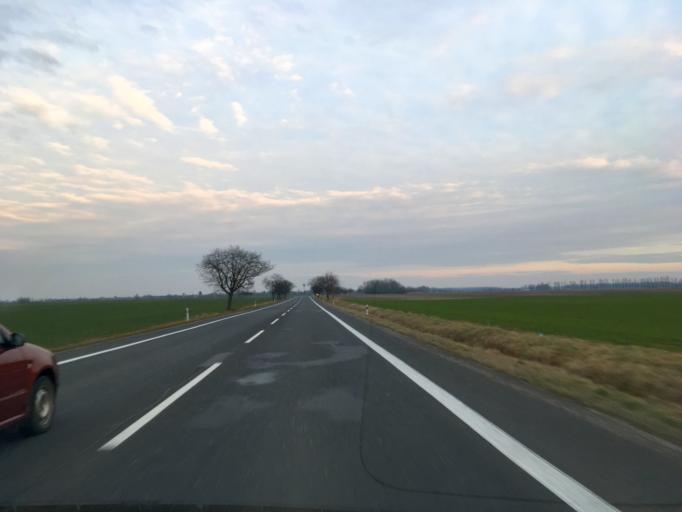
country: HU
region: Komarom-Esztergom
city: Acs
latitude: 47.7763
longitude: 17.9442
